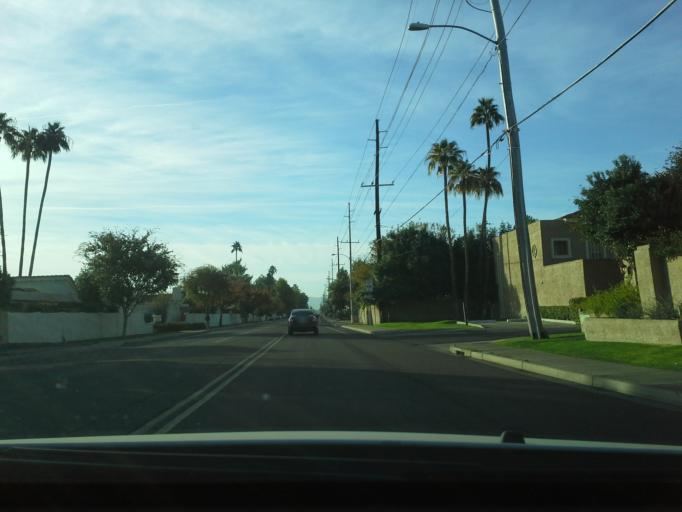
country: US
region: Arizona
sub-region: Maricopa County
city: Phoenix
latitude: 33.5232
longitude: -112.0563
